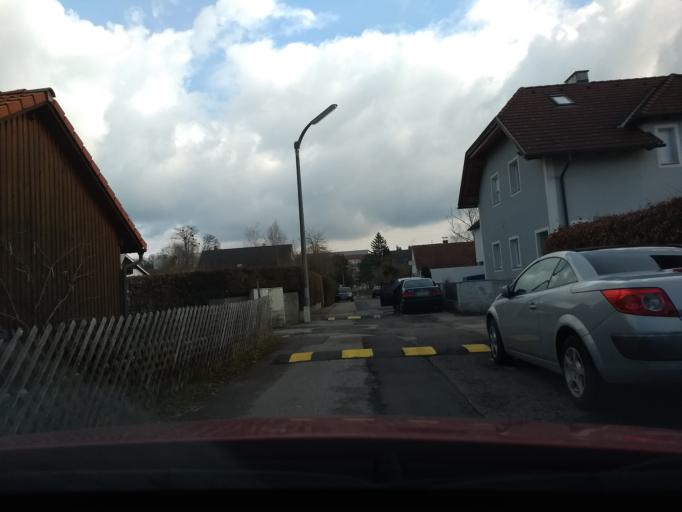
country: AT
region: Upper Austria
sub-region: Politischer Bezirk Steyr-Land
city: Garsten
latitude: 48.0447
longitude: 14.3876
